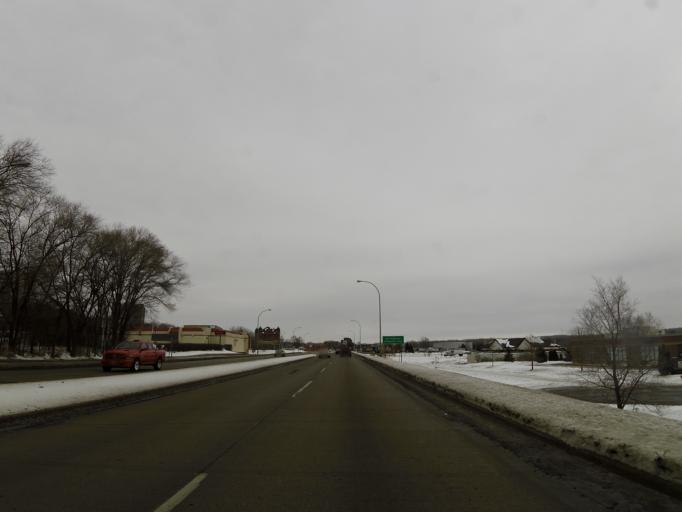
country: US
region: Minnesota
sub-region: Dakota County
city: South Saint Paul
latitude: 44.8891
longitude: -93.0330
